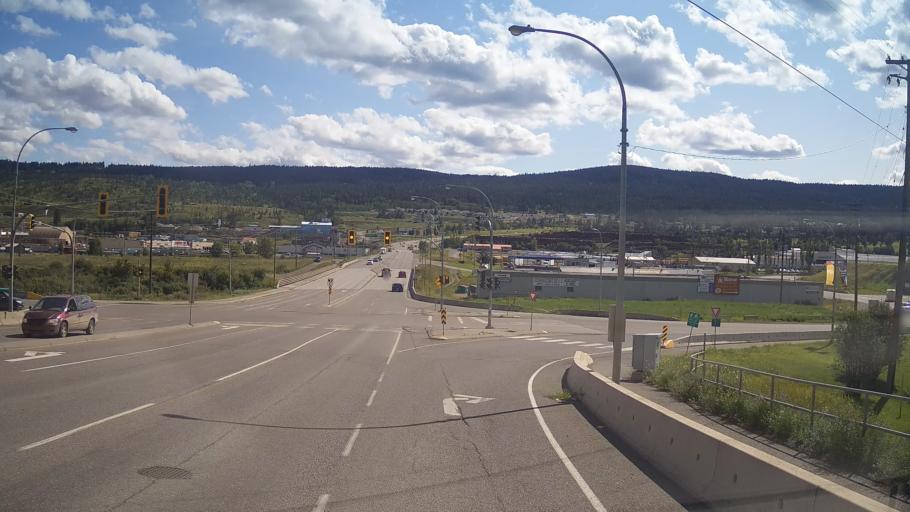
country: CA
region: British Columbia
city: Williams Lake
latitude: 52.1243
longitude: -122.1296
